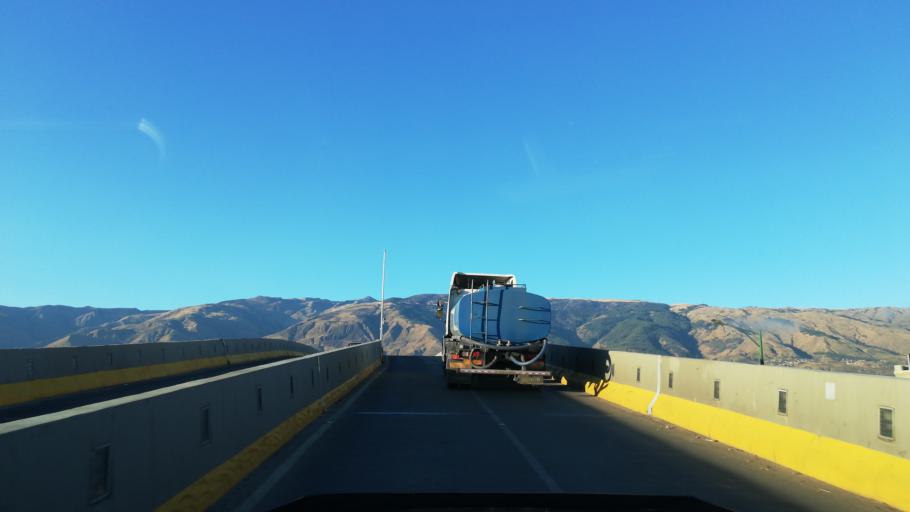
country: BO
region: Cochabamba
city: Cochabamba
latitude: -17.3938
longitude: -66.1846
